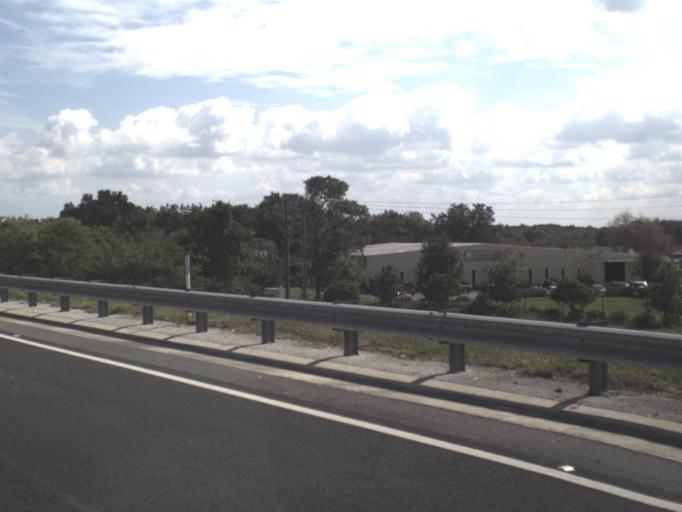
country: US
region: Florida
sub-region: Polk County
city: Crystal Lake
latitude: 28.0043
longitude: -81.8923
